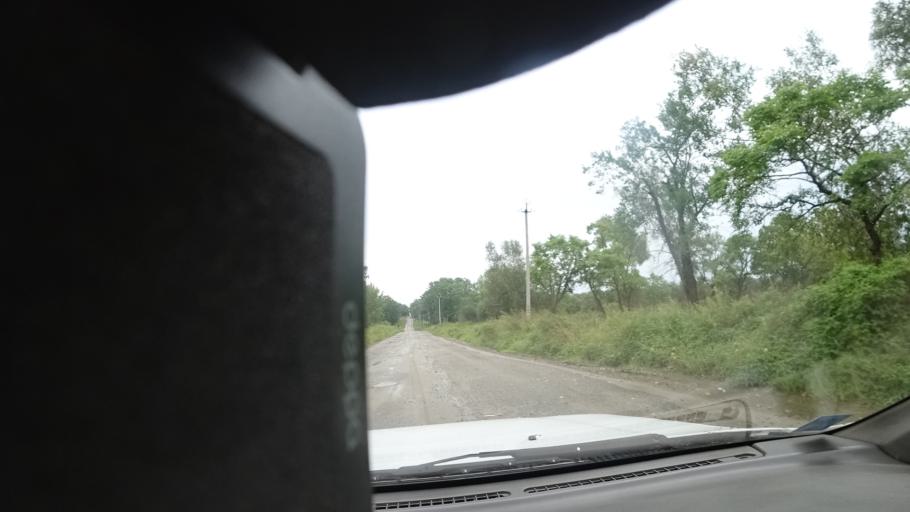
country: RU
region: Primorskiy
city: Lazo
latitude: 45.8699
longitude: 133.6784
